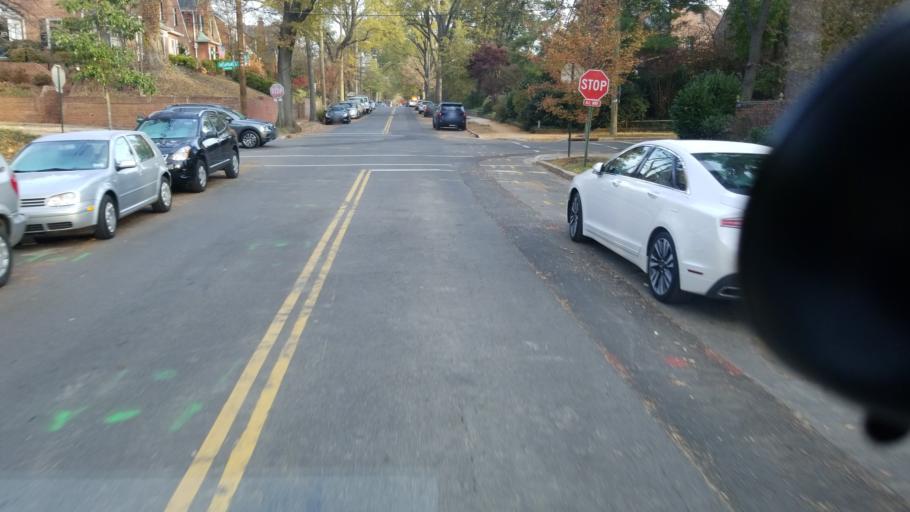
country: US
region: Maryland
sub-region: Montgomery County
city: Friendship Village
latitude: 38.9508
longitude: -77.0906
